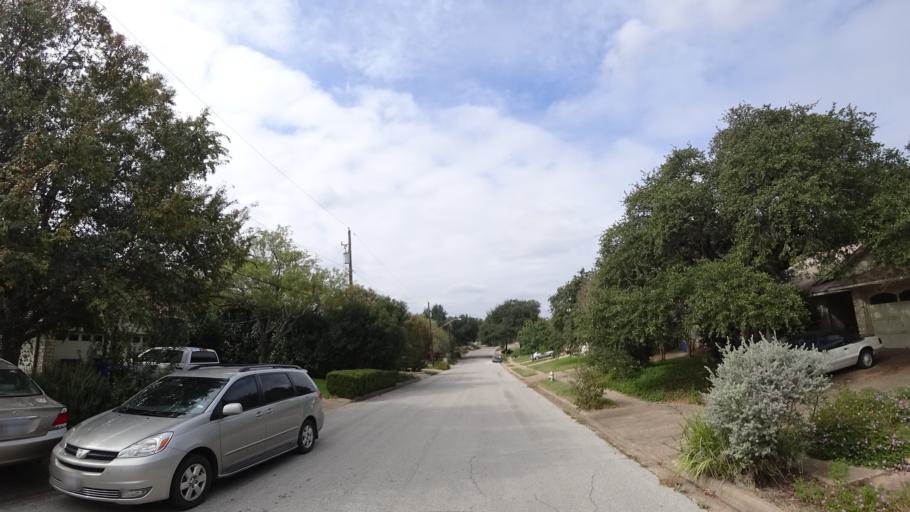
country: US
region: Texas
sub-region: Travis County
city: Wells Branch
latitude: 30.4260
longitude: -97.7075
